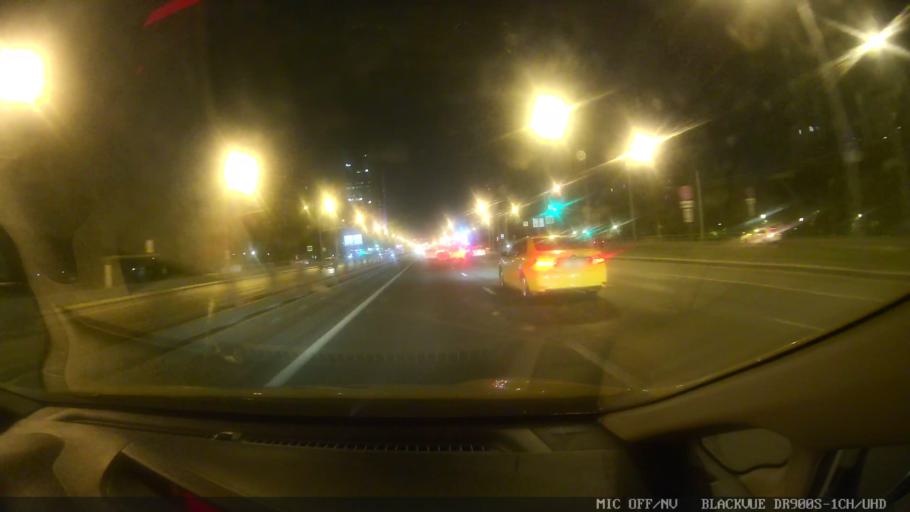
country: RU
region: Moscow
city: Metrogorodok
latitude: 55.8054
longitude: 37.7648
